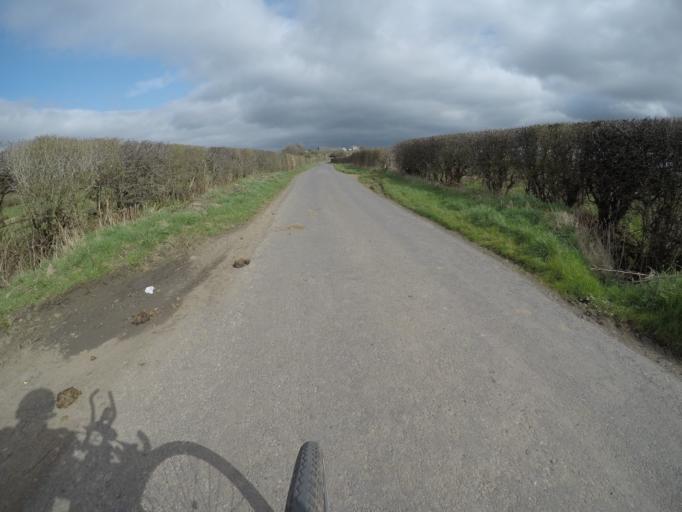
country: GB
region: Scotland
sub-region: North Ayrshire
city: Springside
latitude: 55.6461
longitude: -4.6213
